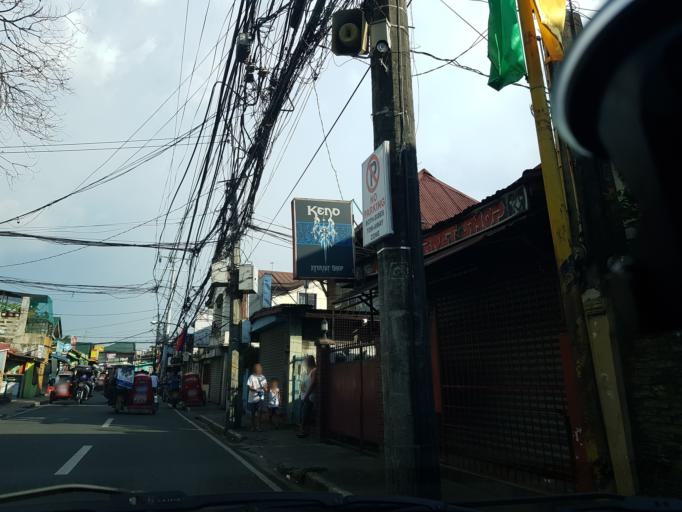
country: PH
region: Metro Manila
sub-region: Marikina
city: Calumpang
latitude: 14.6114
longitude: 121.0853
